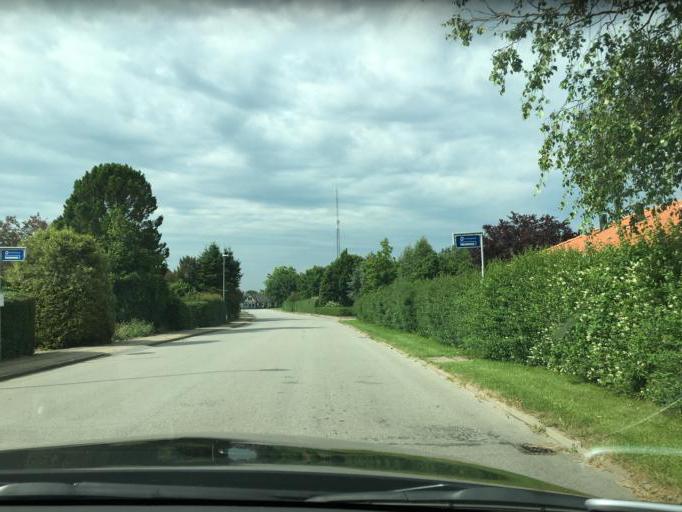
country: DK
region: South Denmark
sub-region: Vejle Kommune
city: Borkop
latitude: 55.6171
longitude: 9.5700
